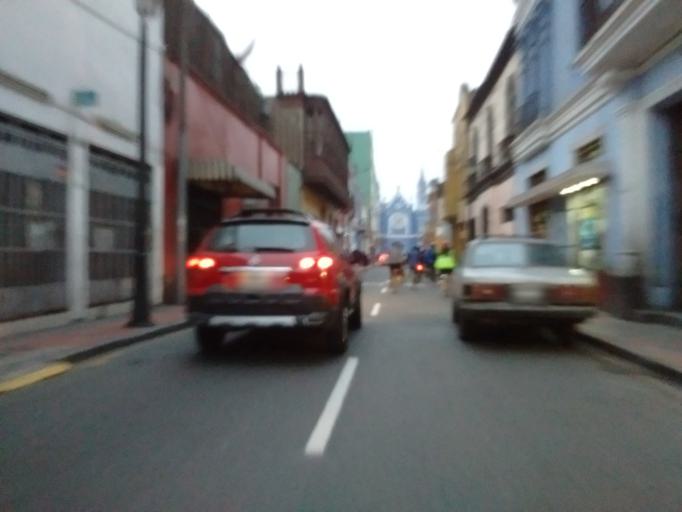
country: PE
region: Lima
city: Lima
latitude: -12.0520
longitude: -77.0370
